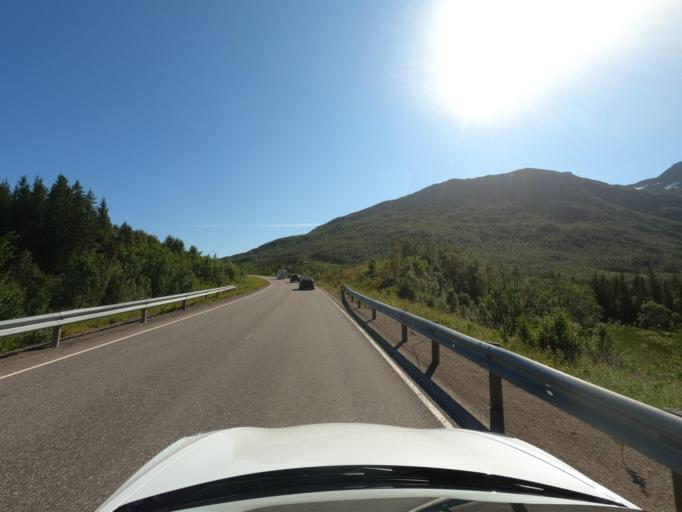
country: NO
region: Nordland
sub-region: Lodingen
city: Lodingen
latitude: 68.5288
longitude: 15.7528
